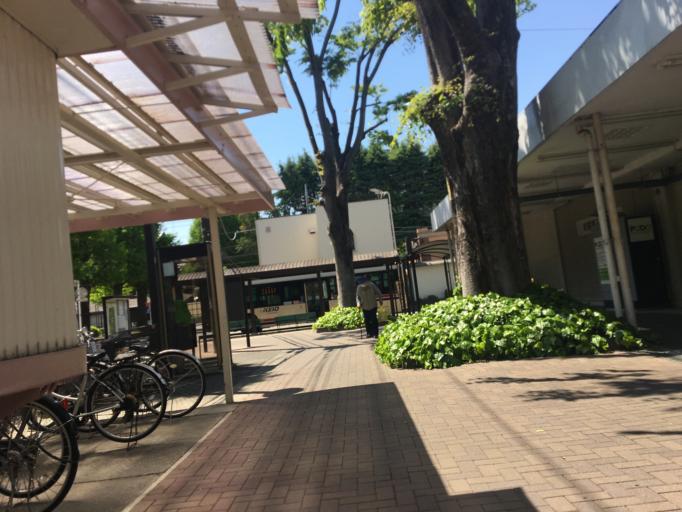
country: JP
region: Tokyo
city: Kokubunji
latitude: 35.7189
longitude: 139.4890
